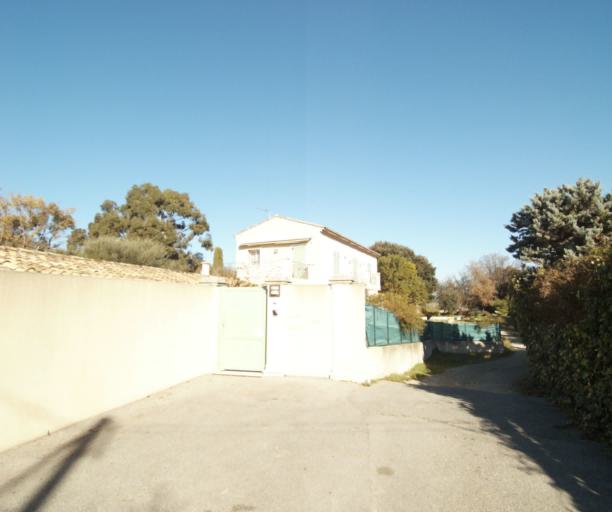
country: FR
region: Provence-Alpes-Cote d'Azur
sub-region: Departement des Alpes-Maritimes
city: Biot
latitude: 43.6079
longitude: 7.1019
